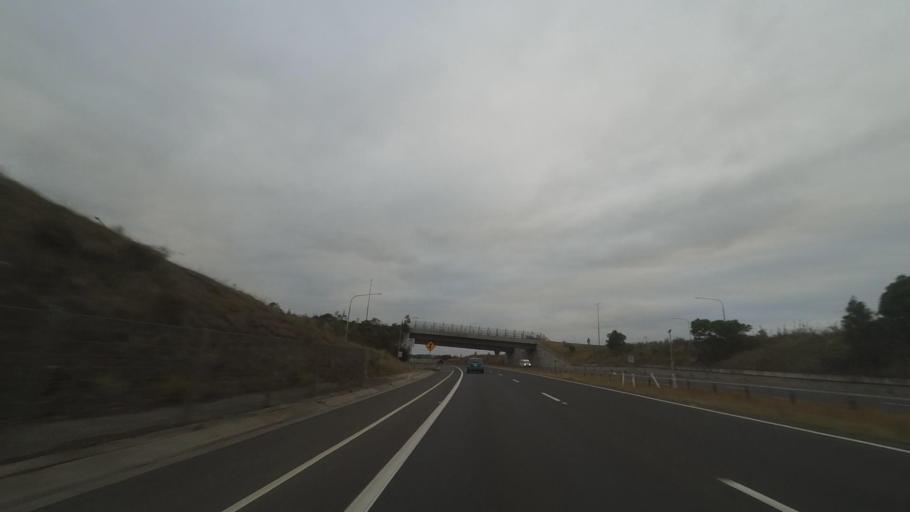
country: AU
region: New South Wales
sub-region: Shellharbour
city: Croom
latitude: -34.5902
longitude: 150.8442
